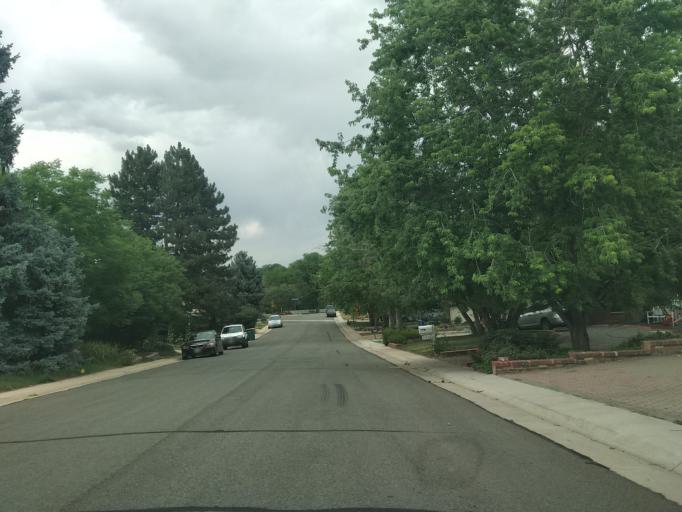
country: US
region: Colorado
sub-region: Jefferson County
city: Lakewood
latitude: 39.6978
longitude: -105.0918
